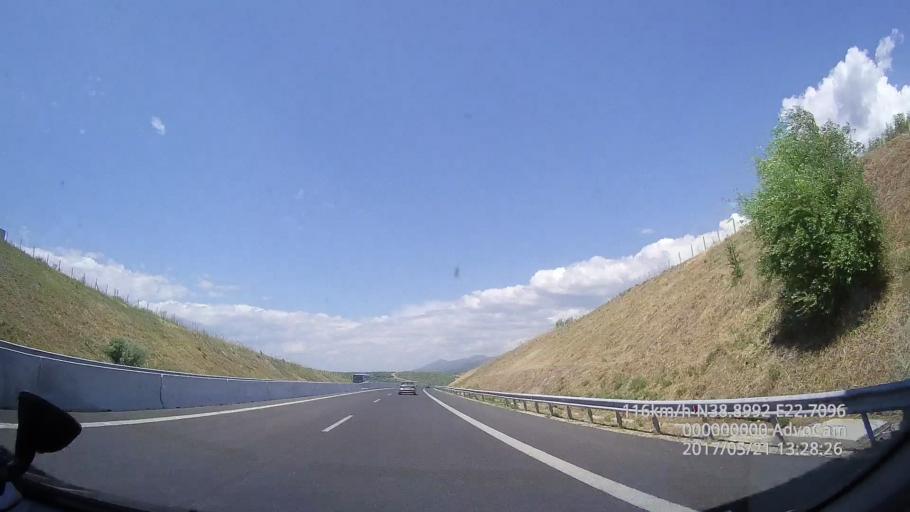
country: GR
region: Central Greece
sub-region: Nomos Fthiotidos
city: Stylida
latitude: 38.8993
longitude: 22.7090
